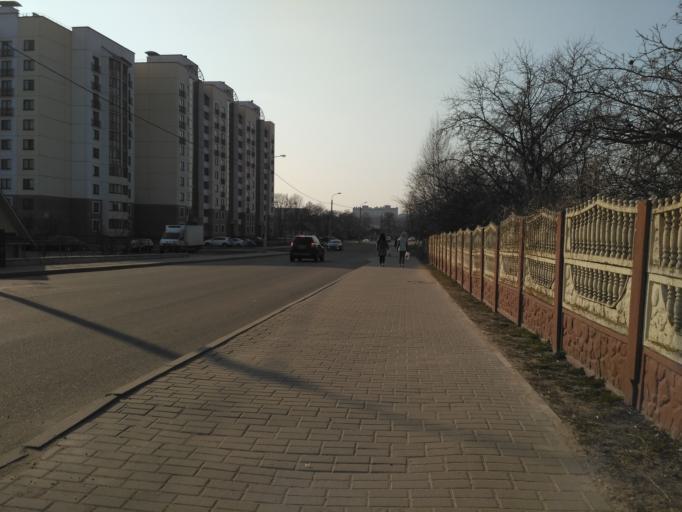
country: BY
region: Minsk
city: Zaslawye
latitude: 54.0081
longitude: 27.2790
